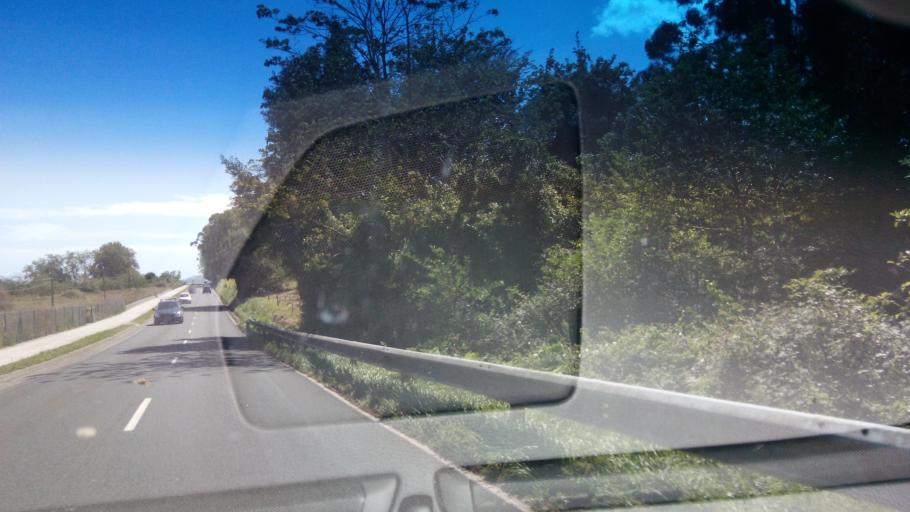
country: ES
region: Asturias
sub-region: Province of Asturias
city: Colunga
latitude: 43.4826
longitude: -5.2446
